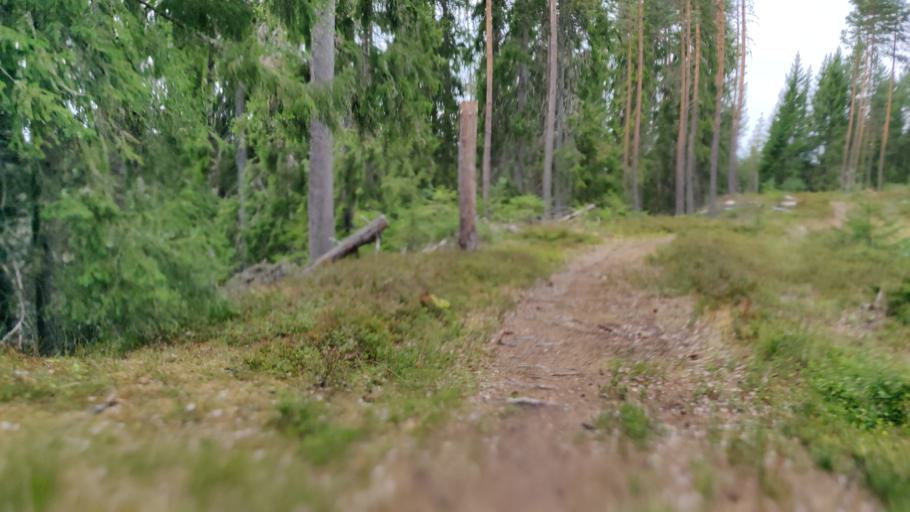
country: SE
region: Vaermland
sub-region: Hagfors Kommun
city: Hagfors
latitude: 60.0222
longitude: 13.5447
